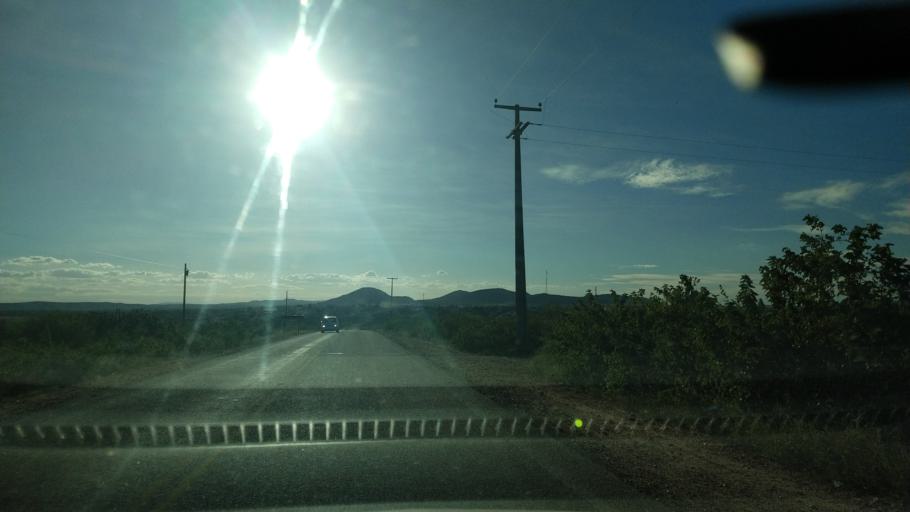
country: BR
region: Rio Grande do Norte
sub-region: Tangara
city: Tangara
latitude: -6.2098
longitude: -35.7908
